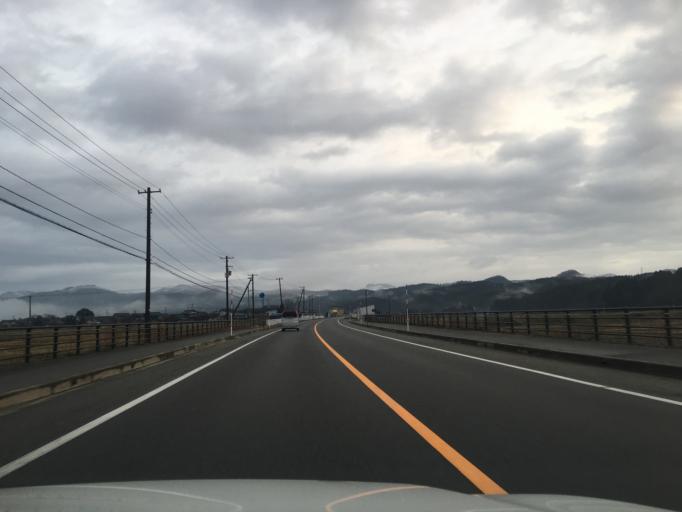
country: JP
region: Niigata
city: Murakami
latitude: 38.3202
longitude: 139.5528
